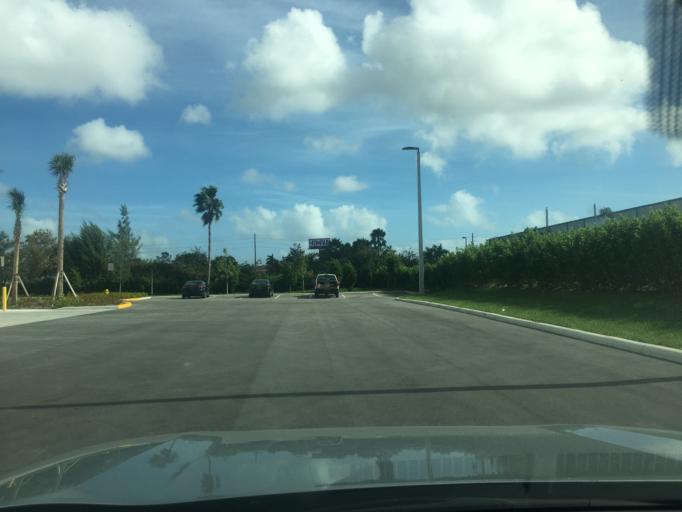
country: US
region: Florida
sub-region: Broward County
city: Broadview Park
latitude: 26.0818
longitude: -80.1790
